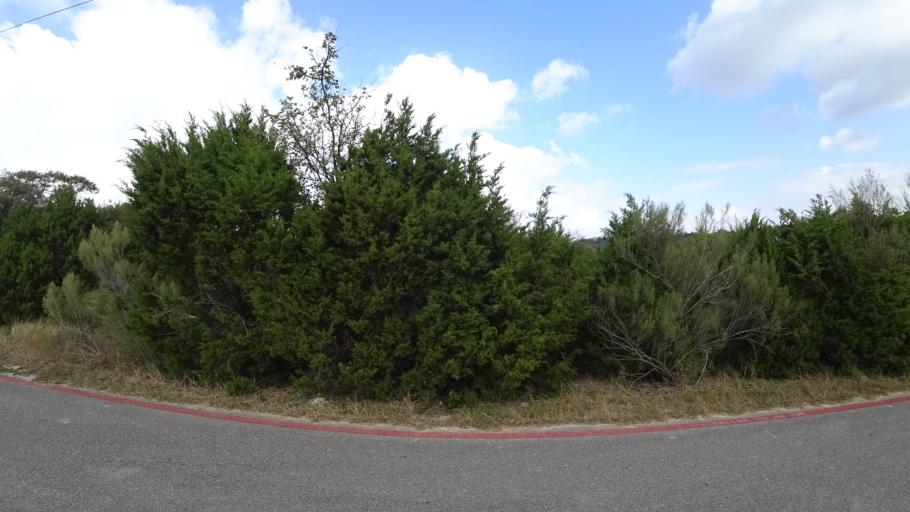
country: US
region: Texas
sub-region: Travis County
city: Barton Creek
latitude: 30.3056
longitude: -97.8837
